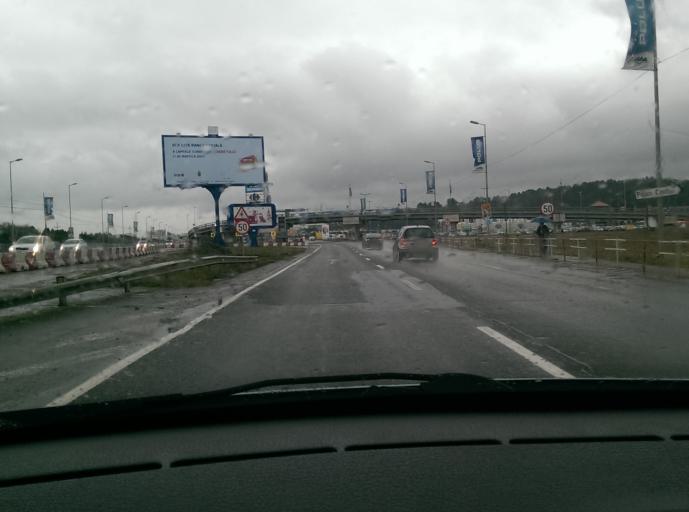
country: RO
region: Cluj
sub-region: Comuna Floresti
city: Floresti
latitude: 46.7532
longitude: 23.5284
